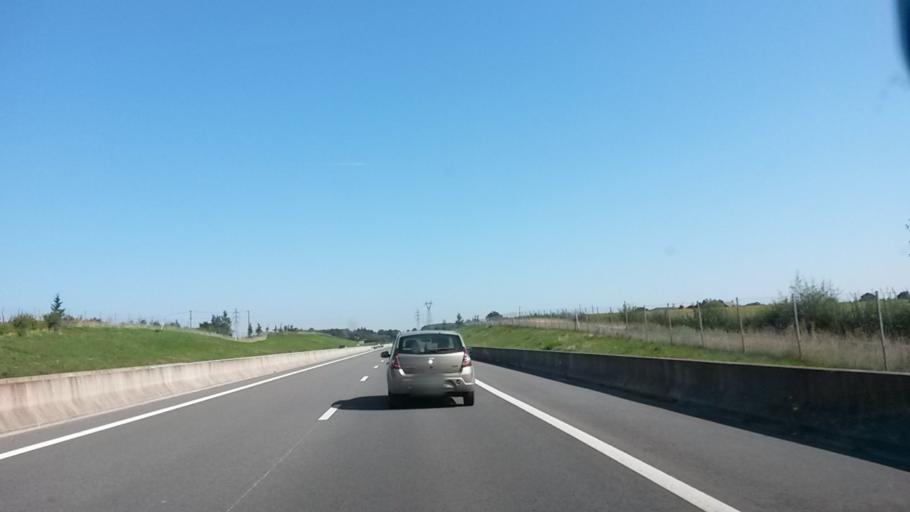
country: FR
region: Nord-Pas-de-Calais
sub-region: Departement du Nord
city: Louvroil
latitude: 50.2239
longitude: 3.9577
